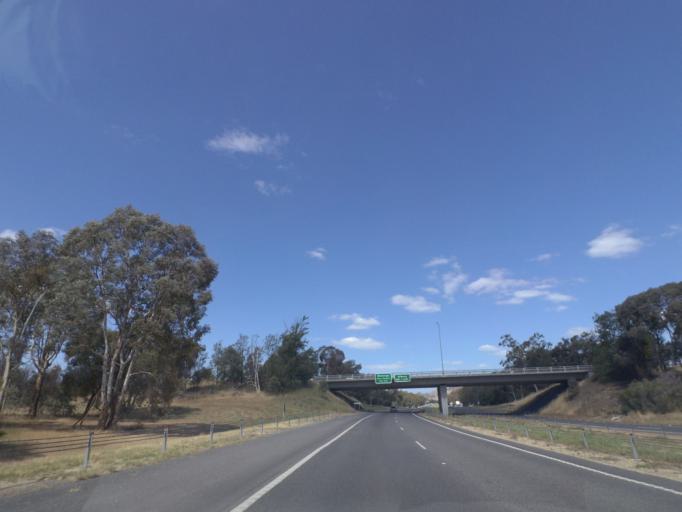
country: AU
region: Victoria
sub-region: Wodonga
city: Wodonga
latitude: -36.1068
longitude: 146.8693
